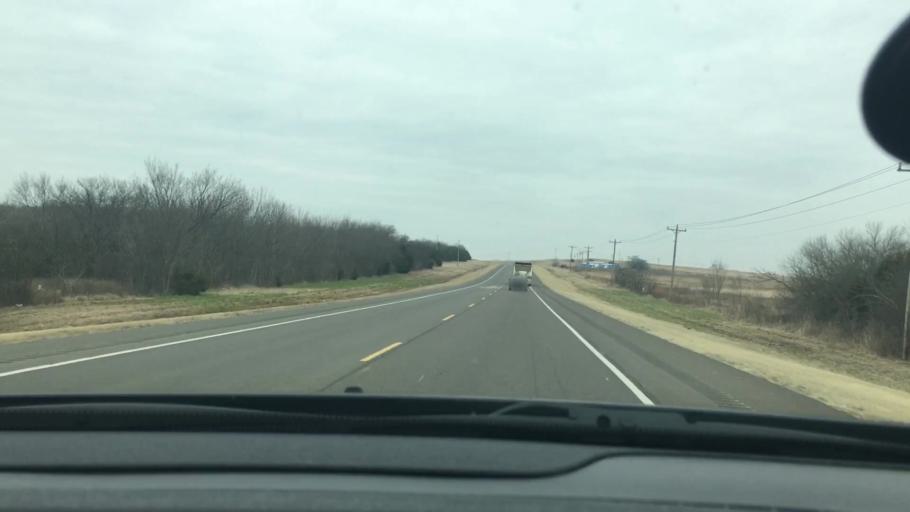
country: US
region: Oklahoma
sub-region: Murray County
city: Davis
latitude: 34.5163
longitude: -97.2053
